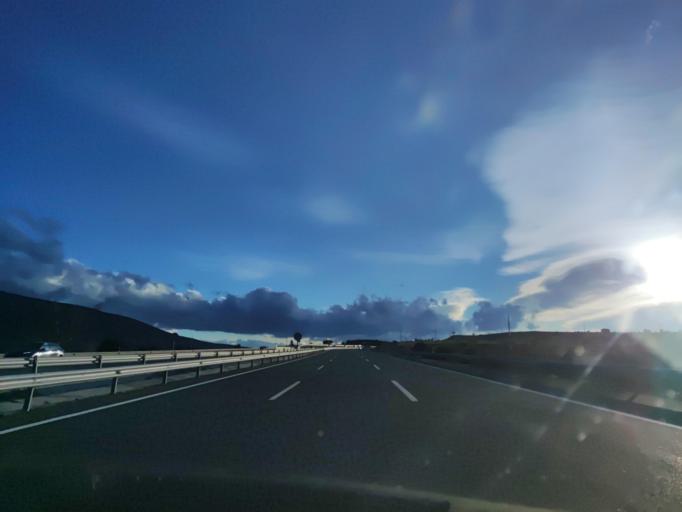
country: ES
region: Castille and Leon
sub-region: Provincia de Segovia
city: Vegas de Matute
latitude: 40.7405
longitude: -4.2598
